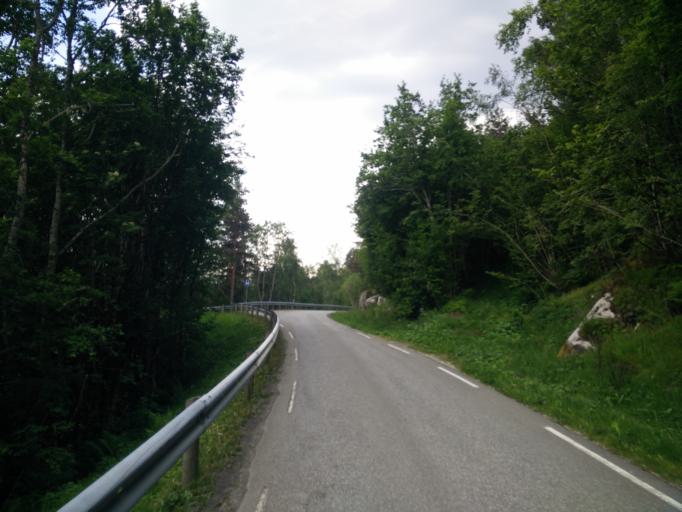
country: NO
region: More og Romsdal
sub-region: Kristiansund
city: Rensvik
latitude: 63.0277
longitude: 7.9535
